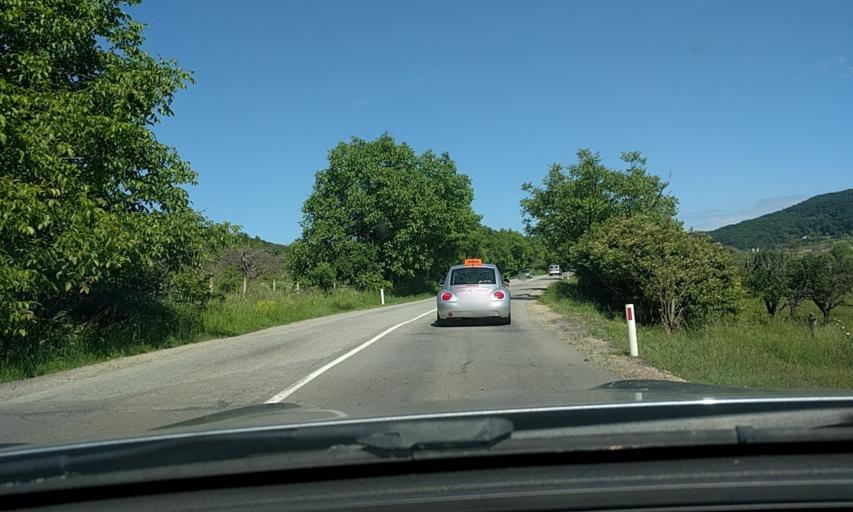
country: RO
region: Bistrita-Nasaud
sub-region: Municipiul Bistrita
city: Unirea
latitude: 47.1729
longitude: 24.4947
